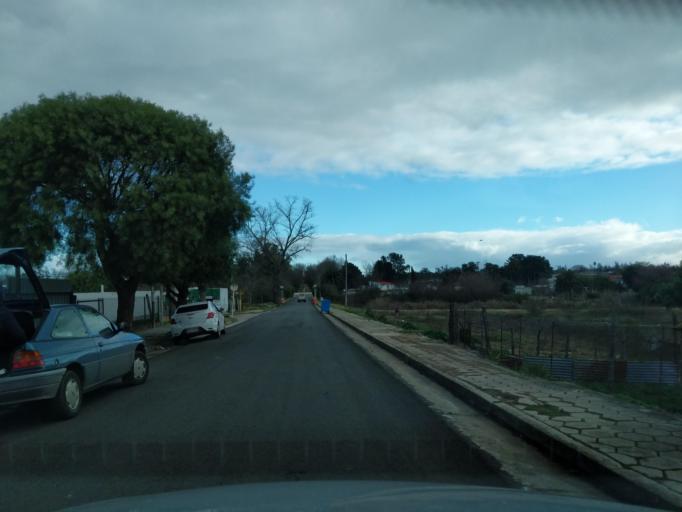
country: UY
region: Florida
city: Florida
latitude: -34.1027
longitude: -56.2220
